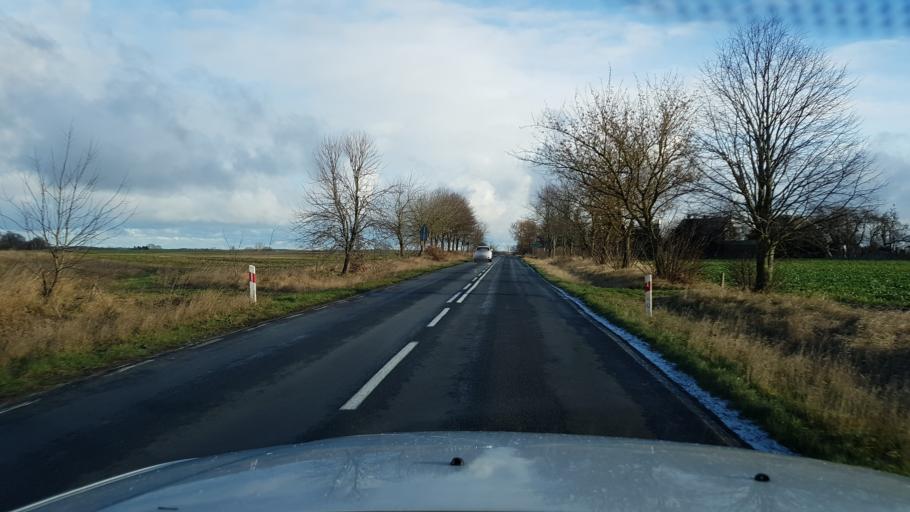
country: PL
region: West Pomeranian Voivodeship
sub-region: Powiat kolobrzeski
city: Grzybowo
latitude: 54.0845
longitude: 15.4542
